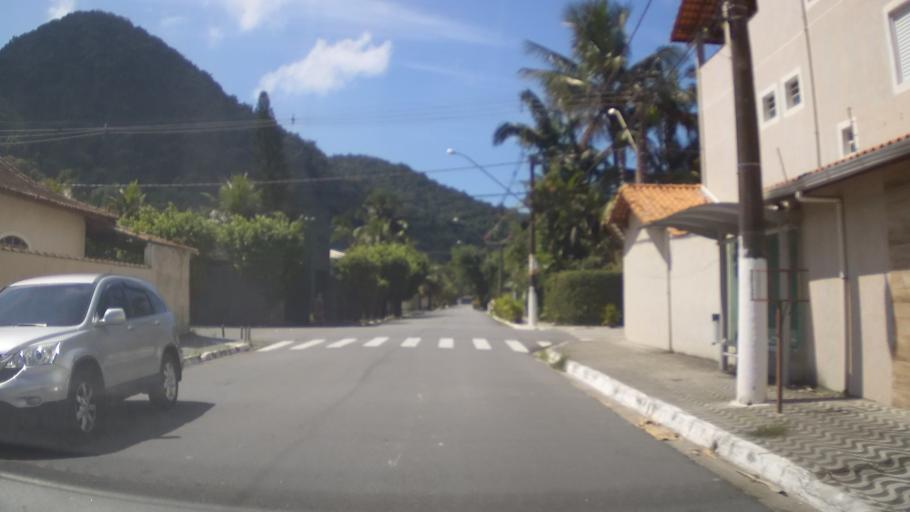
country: BR
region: Sao Paulo
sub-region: Praia Grande
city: Praia Grande
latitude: -24.0040
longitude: -46.4044
